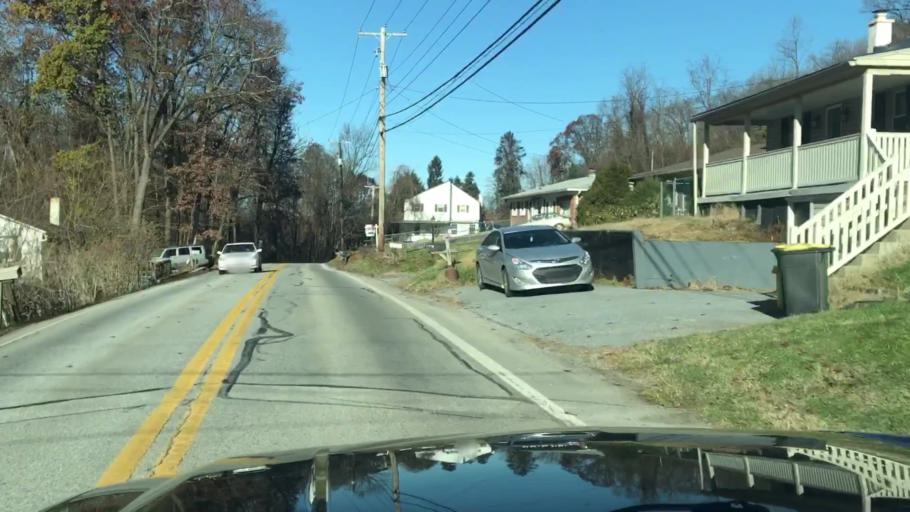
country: US
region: Pennsylvania
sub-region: Cumberland County
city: Lower Allen
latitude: 40.1870
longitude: -76.8876
